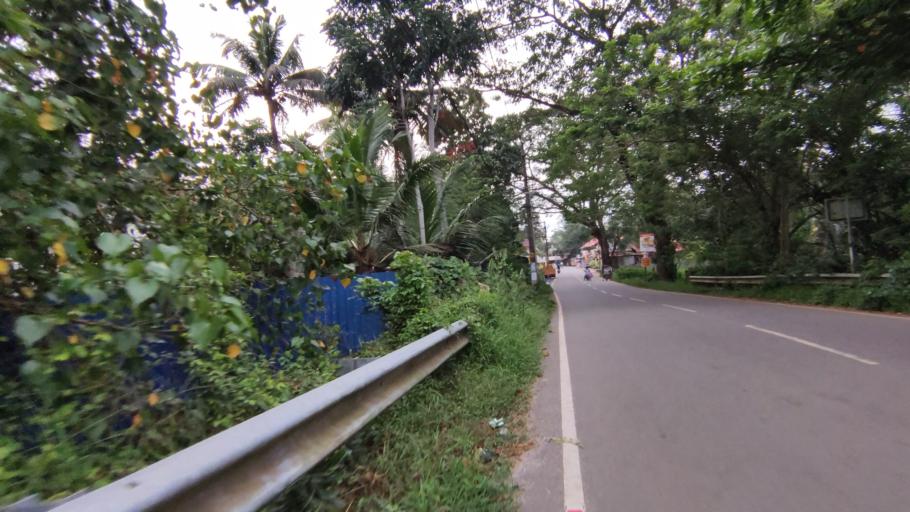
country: IN
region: Kerala
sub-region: Alappuzha
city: Shertallai
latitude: 9.6570
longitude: 76.3674
